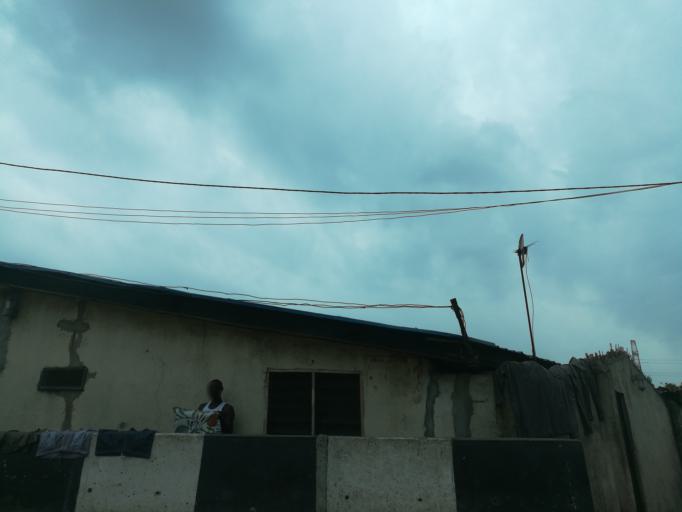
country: NG
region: Lagos
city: Ojota
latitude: 6.6124
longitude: 3.3972
